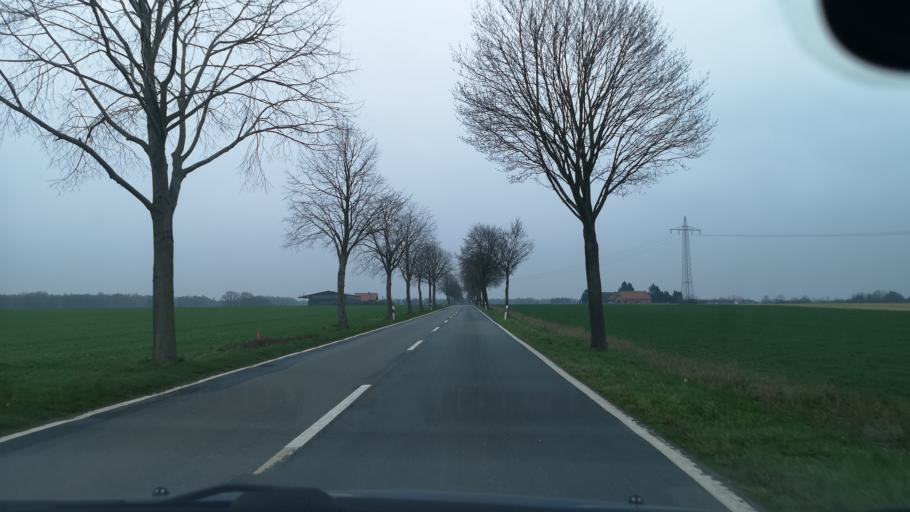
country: DE
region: Lower Saxony
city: Neustadt am Rubenberge
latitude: 52.5564
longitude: 9.4278
